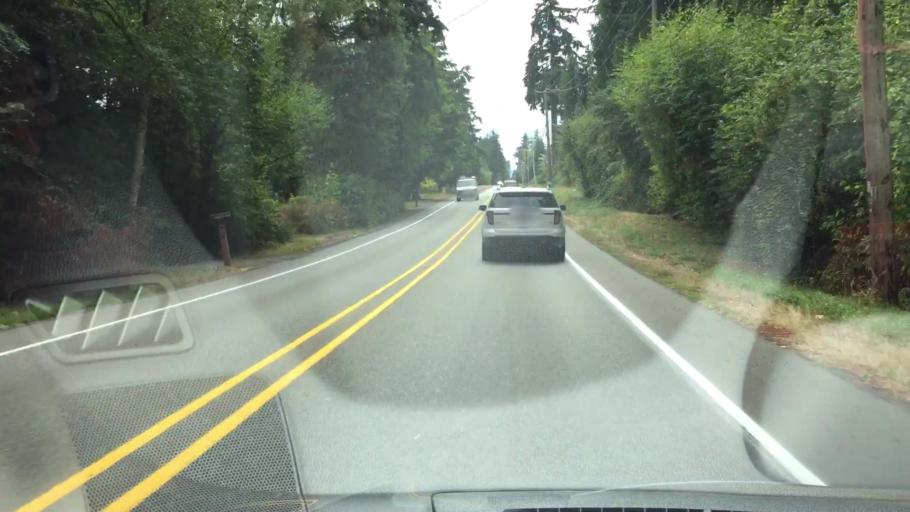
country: US
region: Washington
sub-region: Pierce County
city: South Hill
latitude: 47.1305
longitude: -122.2665
